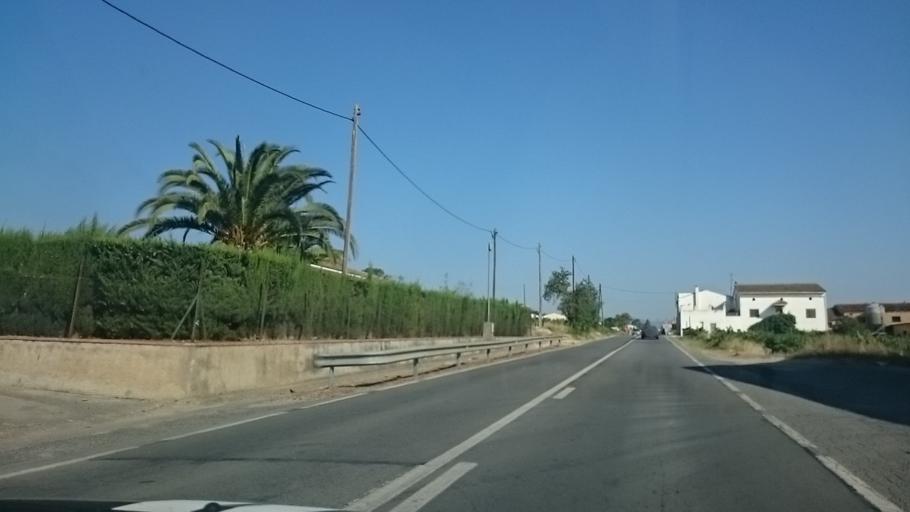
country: ES
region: Catalonia
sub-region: Provincia de Barcelona
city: Vilobi del Penedes
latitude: 41.3559
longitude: 1.6663
